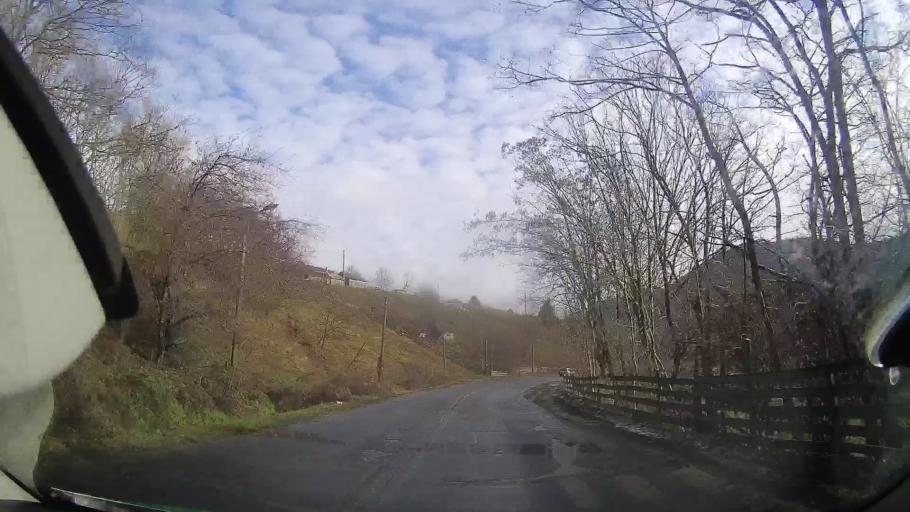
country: RO
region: Alba
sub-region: Comuna Bistra
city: Bistra
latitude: 46.3749
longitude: 23.1055
